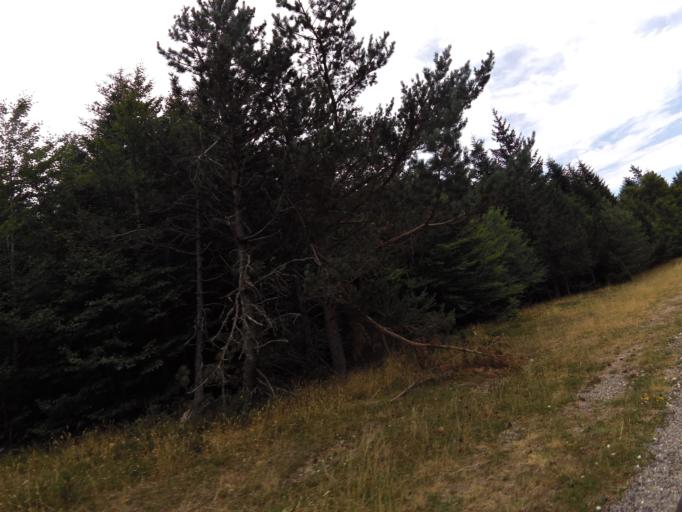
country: FR
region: Languedoc-Roussillon
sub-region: Departement du Gard
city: Valleraugue
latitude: 44.0828
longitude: 3.5685
